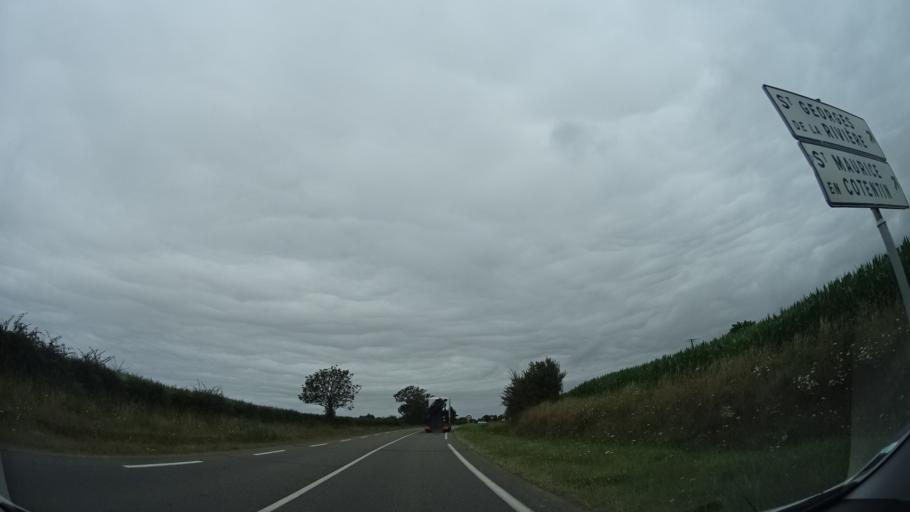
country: FR
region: Lower Normandy
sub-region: Departement de la Manche
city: Portbail
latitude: 49.3670
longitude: -1.7205
